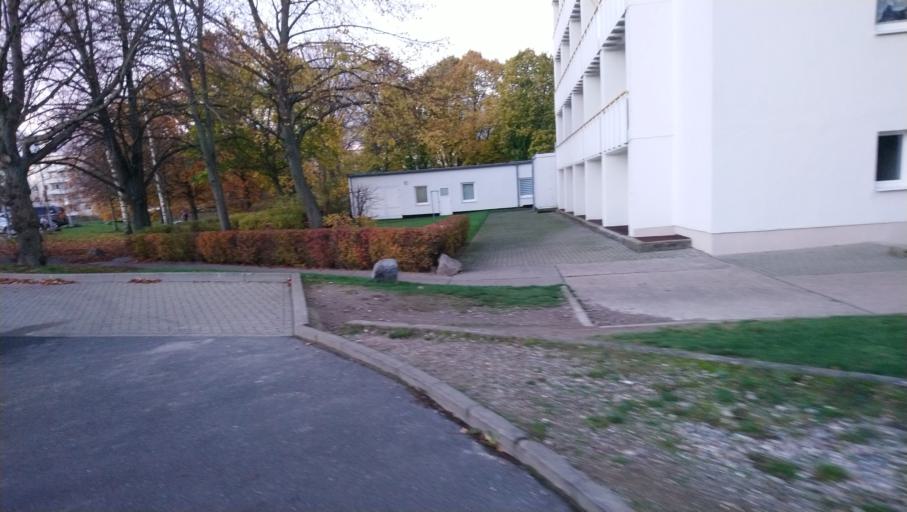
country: DE
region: Mecklenburg-Vorpommern
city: Rostock
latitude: 54.0713
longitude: 12.1186
